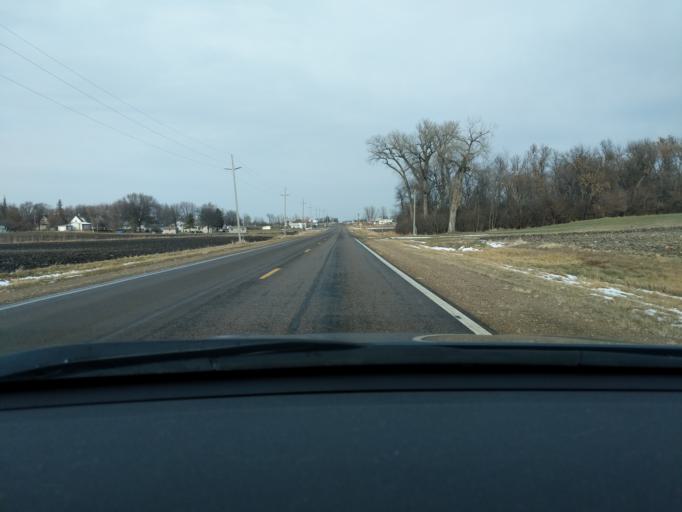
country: US
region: Minnesota
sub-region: Renville County
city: Renville
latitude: 44.7830
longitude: -95.3409
